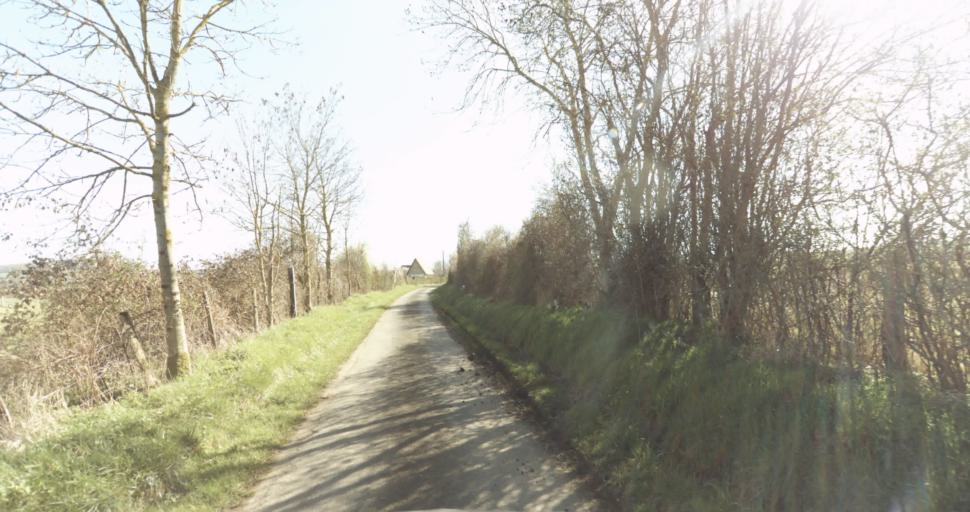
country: FR
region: Lower Normandy
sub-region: Departement du Calvados
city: Saint-Pierre-sur-Dives
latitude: 49.0310
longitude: 0.0199
